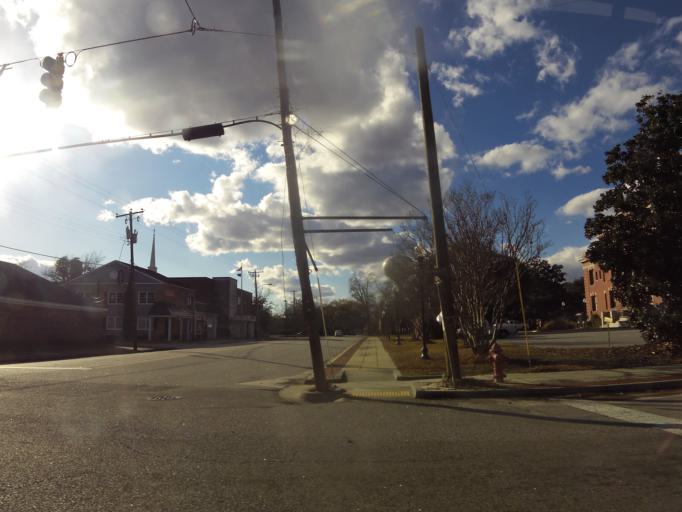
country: US
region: South Carolina
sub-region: Clarendon County
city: Manning
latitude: 33.6942
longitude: -80.2107
